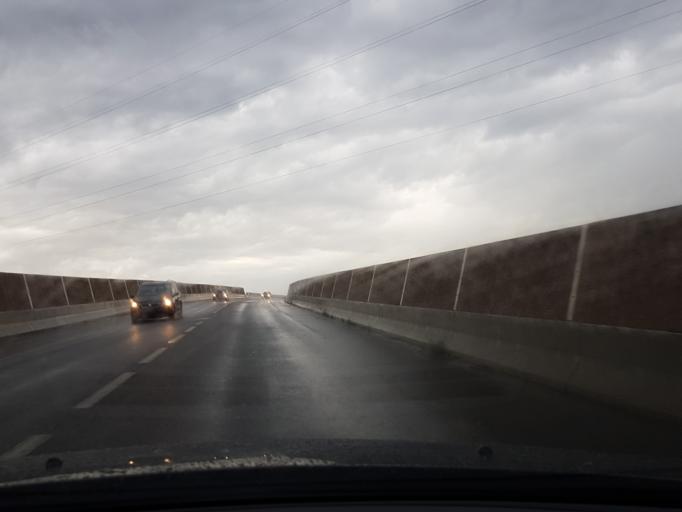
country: FR
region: Provence-Alpes-Cote d'Azur
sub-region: Departement du Vaucluse
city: Carpentras
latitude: 44.0361
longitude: 5.0320
